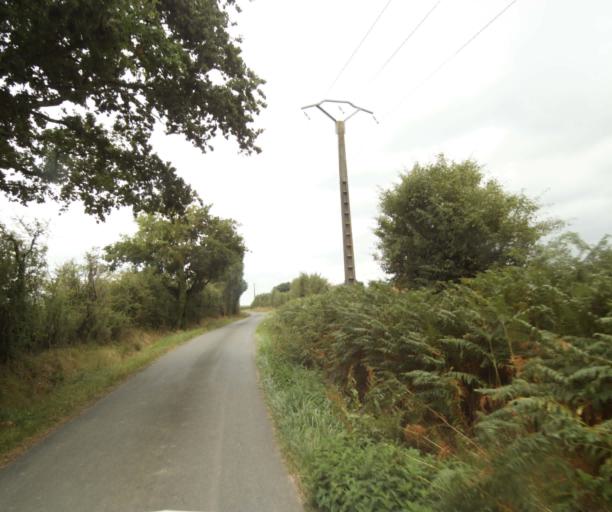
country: FR
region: Pays de la Loire
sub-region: Departement de la Sarthe
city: Juigne-sur-Sarthe
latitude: 47.8455
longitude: -0.2655
